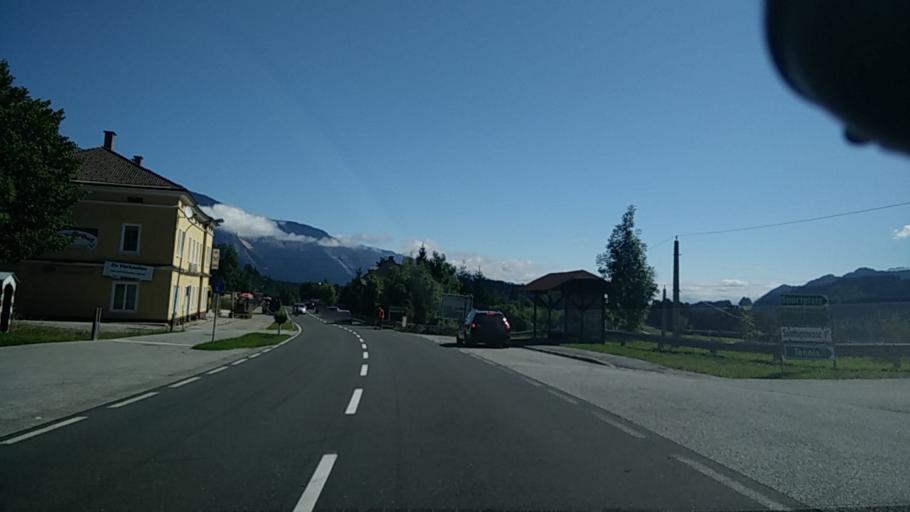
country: AT
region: Carinthia
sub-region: Politischer Bezirk Villach Land
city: Hohenthurn
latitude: 46.5424
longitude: 13.6506
